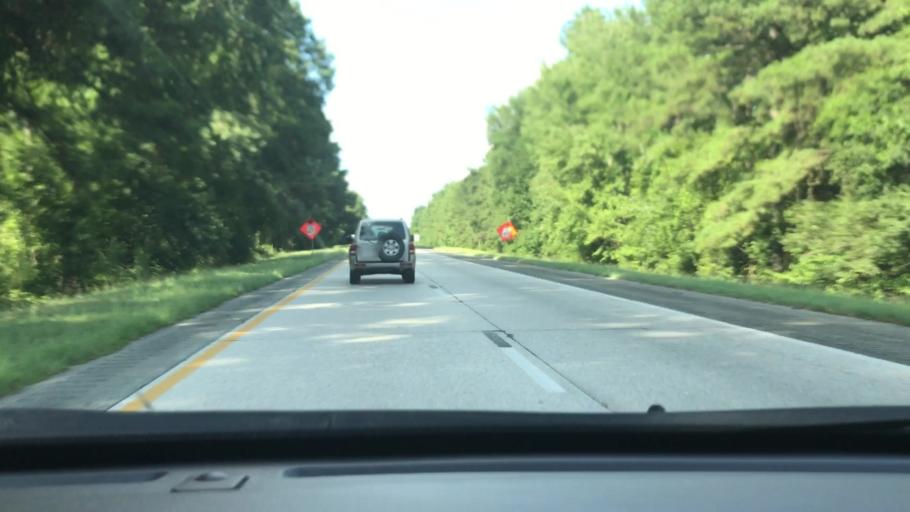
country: US
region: South Carolina
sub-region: Florence County
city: Timmonsville
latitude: 34.0972
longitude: -79.9265
